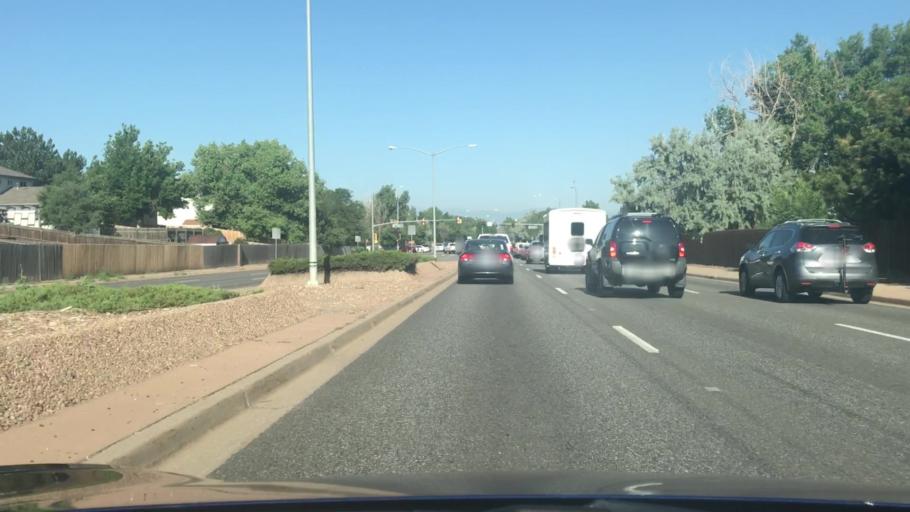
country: US
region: Colorado
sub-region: Arapahoe County
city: Dove Valley
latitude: 39.6531
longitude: -104.7892
